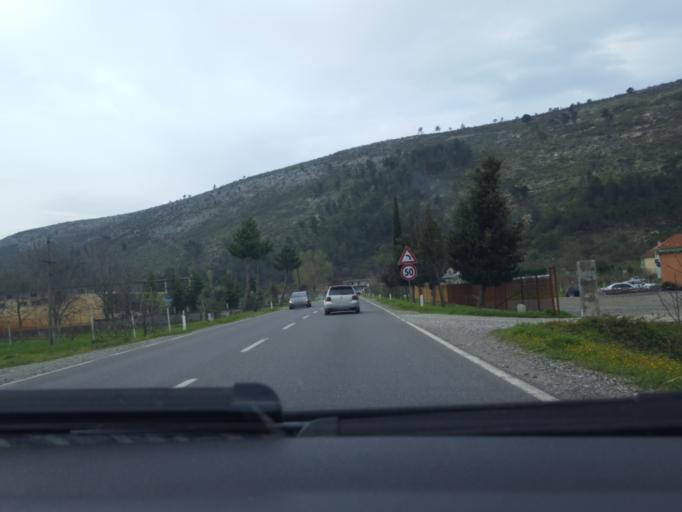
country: AL
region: Lezhe
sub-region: Rrethi i Lezhes
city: Balldreni i Ri
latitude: 41.8048
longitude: 19.6317
